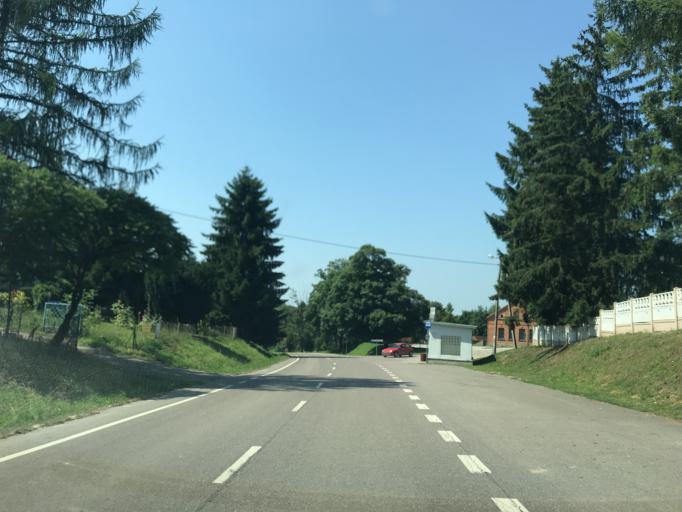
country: PL
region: Kujawsko-Pomorskie
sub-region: Powiat golubsko-dobrzynski
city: Zbojno
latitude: 52.9997
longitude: 19.2150
